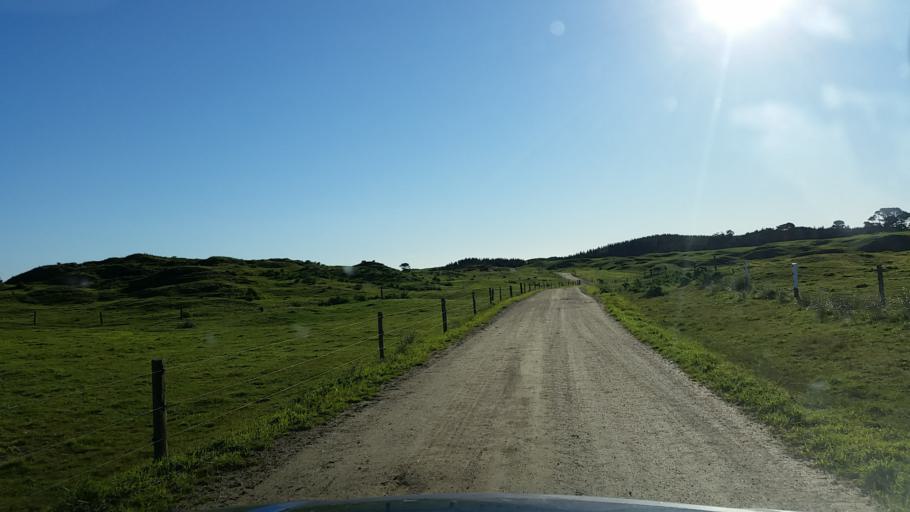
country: NZ
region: Taranaki
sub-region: South Taranaki District
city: Patea
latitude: -39.8377
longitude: 174.6928
